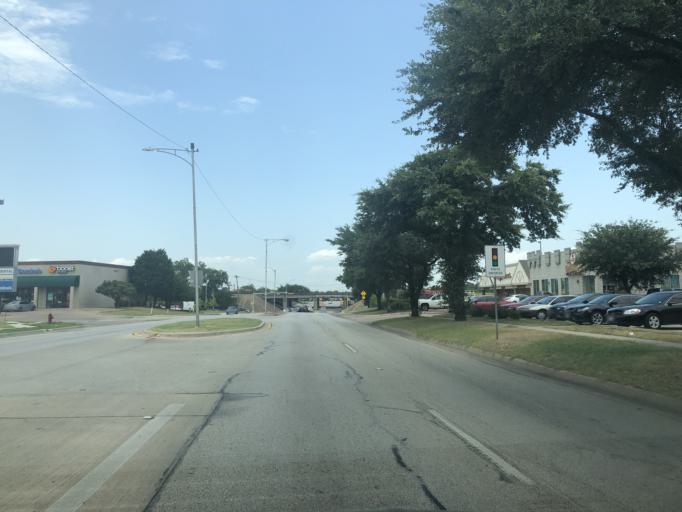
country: US
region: Texas
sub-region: Dallas County
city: Grand Prairie
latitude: 32.7401
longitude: -97.0147
